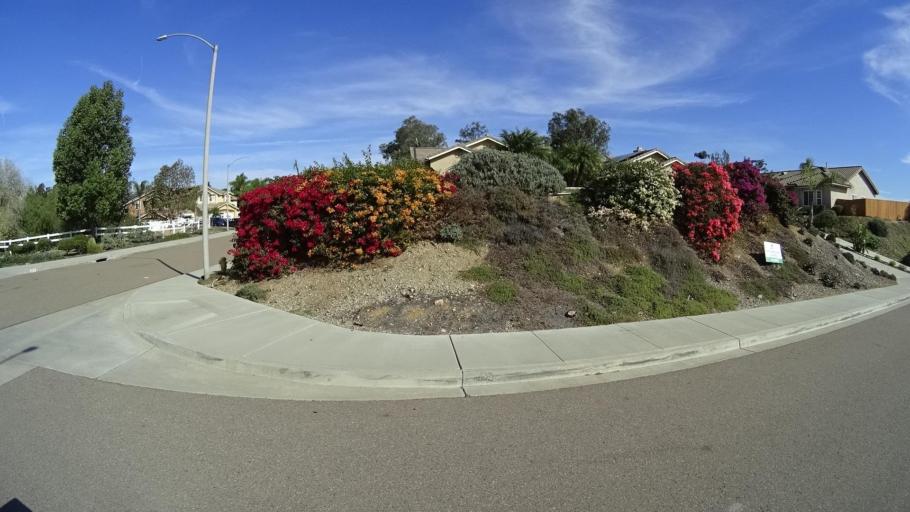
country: US
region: California
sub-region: San Diego County
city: Spring Valley
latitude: 32.7303
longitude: -116.9875
